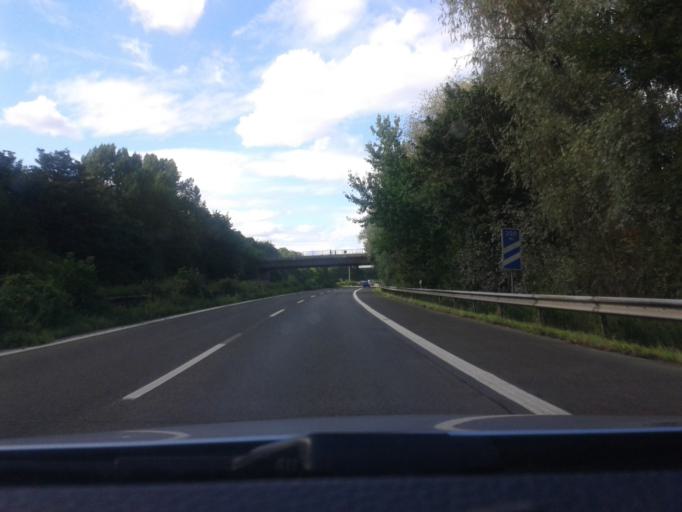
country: DE
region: North Rhine-Westphalia
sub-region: Regierungsbezirk Dusseldorf
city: Moers
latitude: 51.4311
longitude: 6.6727
